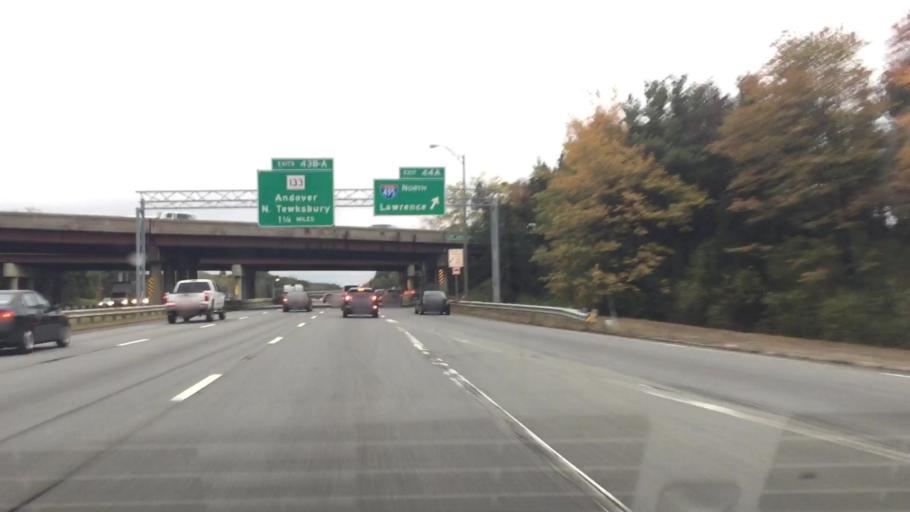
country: US
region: Massachusetts
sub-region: Essex County
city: Lawrence
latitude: 42.6679
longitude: -71.1962
